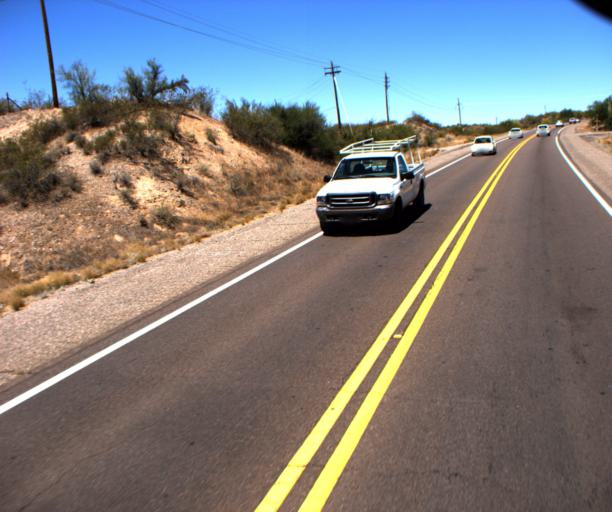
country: US
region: Arizona
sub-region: Maricopa County
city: Wickenburg
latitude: 33.9924
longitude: -112.7509
